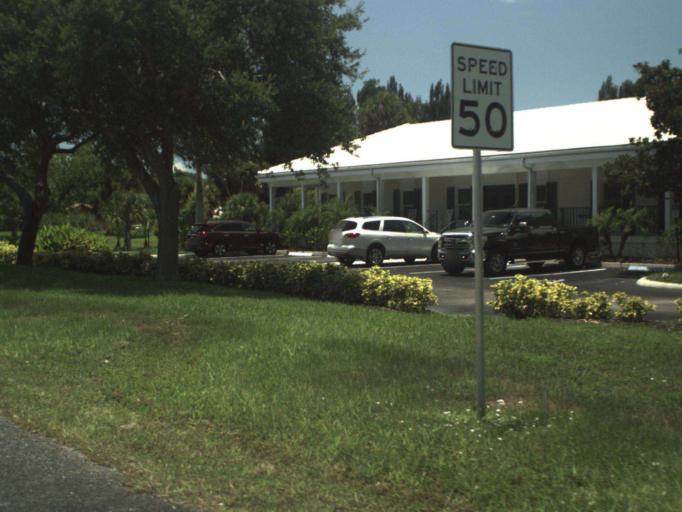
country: US
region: Florida
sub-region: Indian River County
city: Wabasso Beach
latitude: 27.7621
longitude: -80.4412
